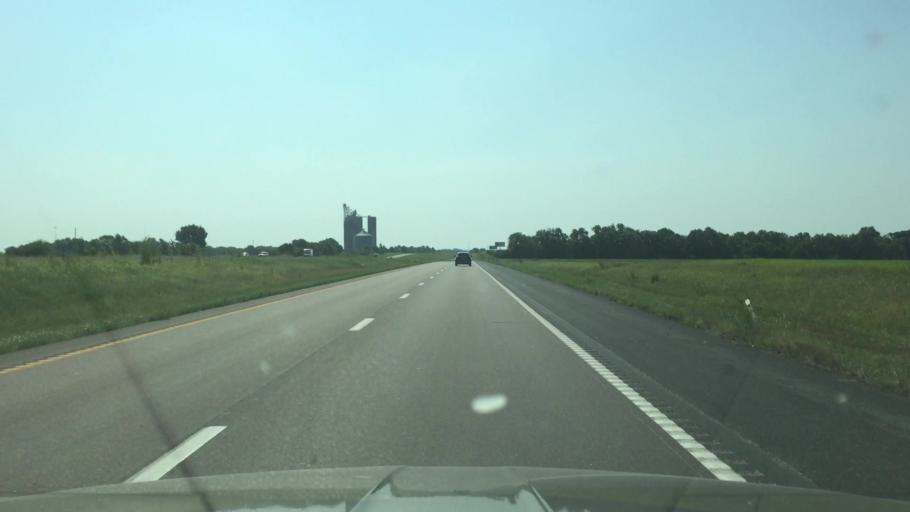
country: US
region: Missouri
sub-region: Pettis County
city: La Monte
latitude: 38.7544
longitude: -93.3589
